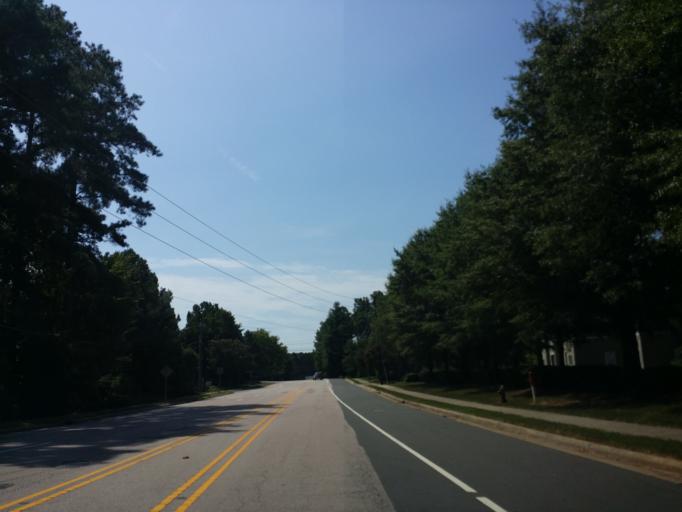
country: US
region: North Carolina
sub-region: Wake County
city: Cary
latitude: 35.8764
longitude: -78.7273
